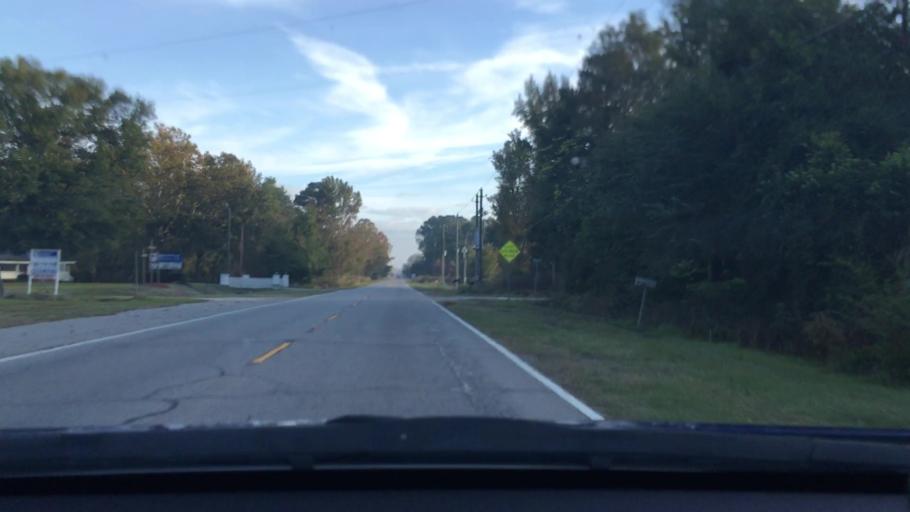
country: US
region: South Carolina
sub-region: Sumter County
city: East Sumter
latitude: 33.9435
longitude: -80.3151
